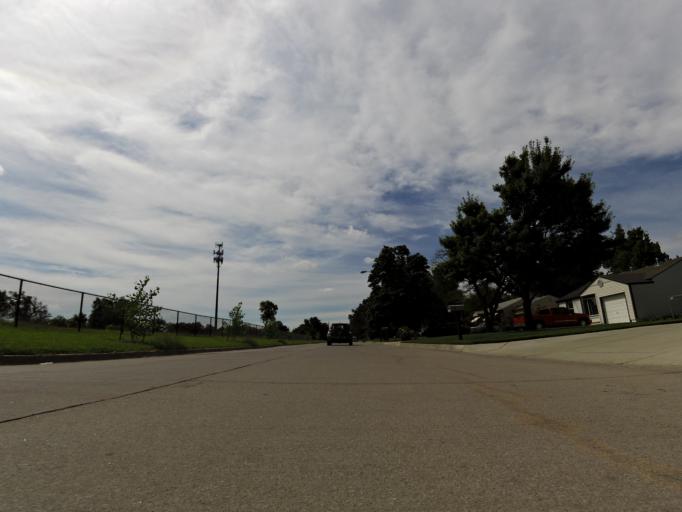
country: US
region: Kansas
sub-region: Sedgwick County
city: Wichita
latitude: 37.7043
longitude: -97.2917
